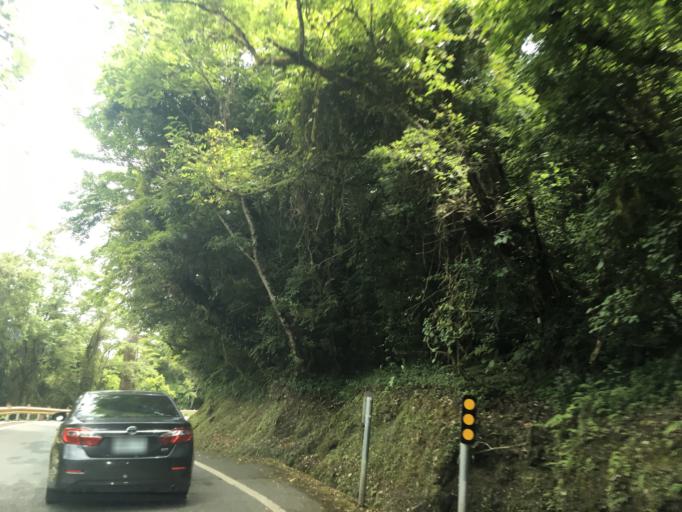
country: TW
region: Taiwan
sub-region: Hualien
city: Hualian
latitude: 24.1769
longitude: 121.3871
